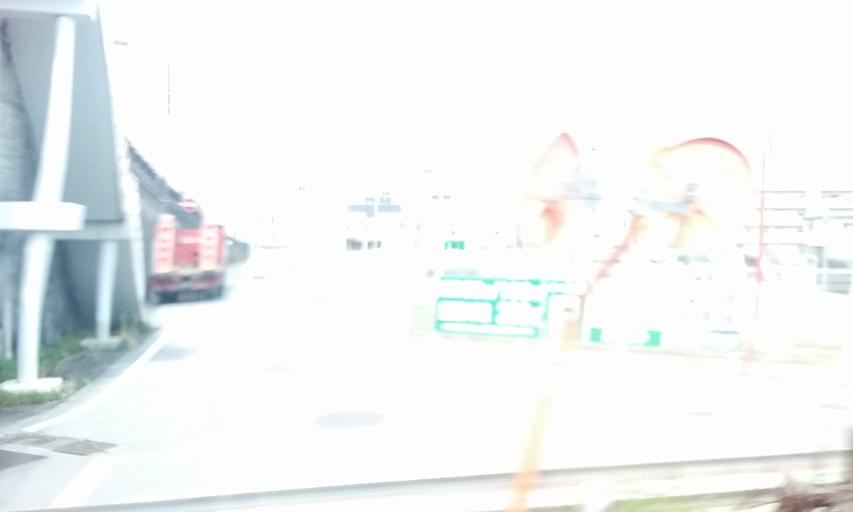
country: JP
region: Shiga Prefecture
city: Hikone
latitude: 35.2682
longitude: 136.2623
